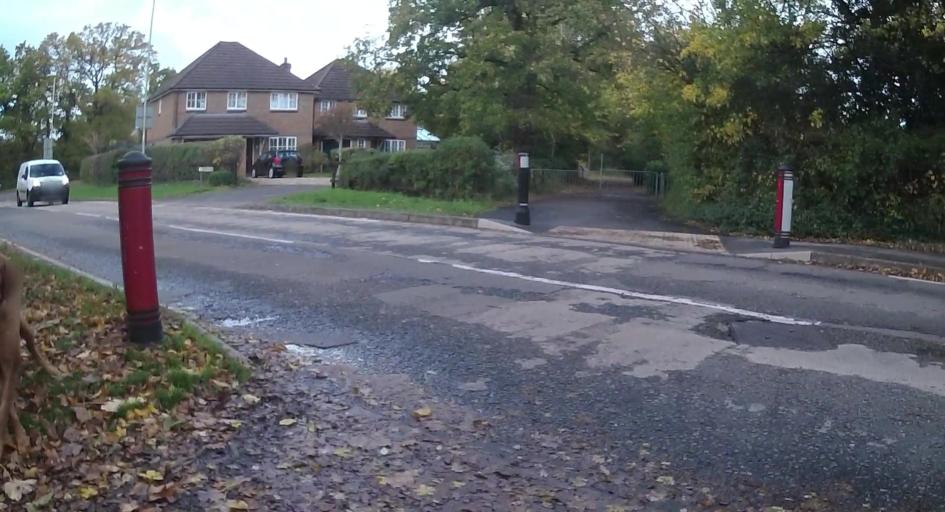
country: GB
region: England
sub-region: Hampshire
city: Old Basing
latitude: 51.2964
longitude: -1.0555
